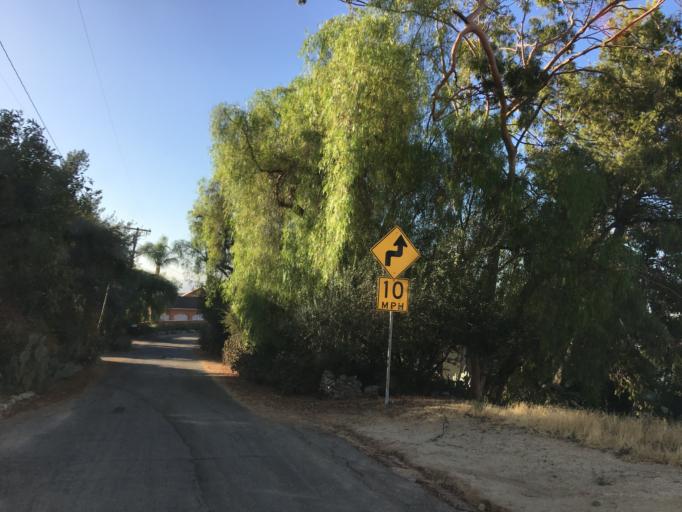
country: US
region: California
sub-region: Los Angeles County
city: San Fernando
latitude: 34.2858
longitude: -118.3775
